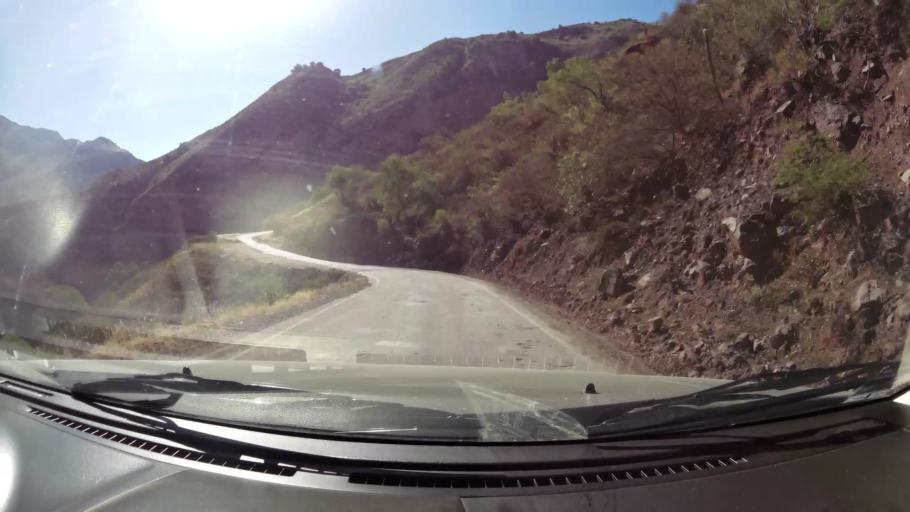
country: PE
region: Huancavelica
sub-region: Provincia de Acobamba
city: Pomacocha
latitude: -12.7880
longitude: -74.4880
